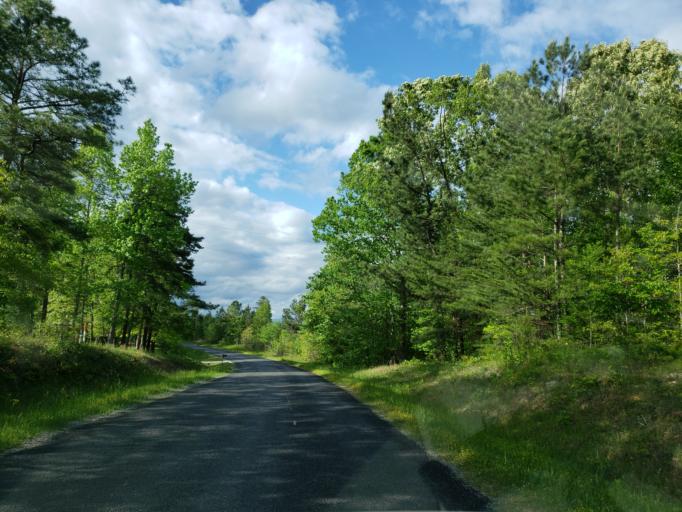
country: US
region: Georgia
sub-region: Haralson County
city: Tallapoosa
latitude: 33.8005
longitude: -85.3797
